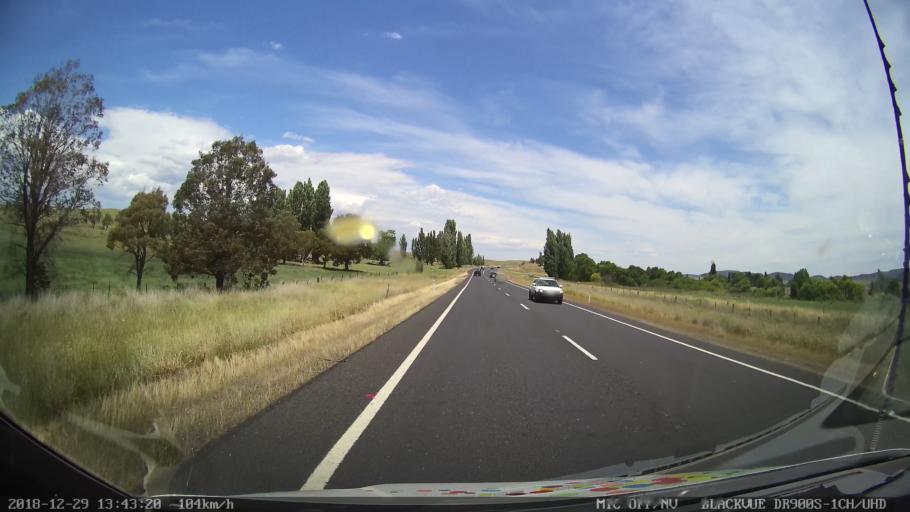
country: AU
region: New South Wales
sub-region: Cooma-Monaro
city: Cooma
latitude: -36.0709
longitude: 149.1594
